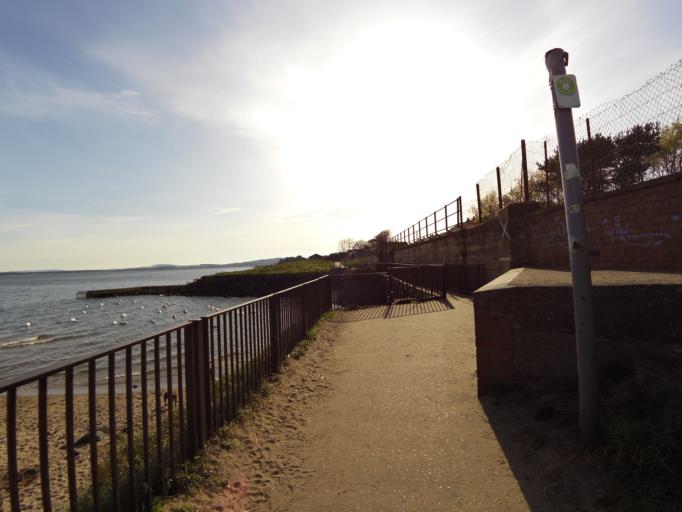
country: GB
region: Scotland
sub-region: Fife
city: Tayport
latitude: 56.4752
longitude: -2.8363
